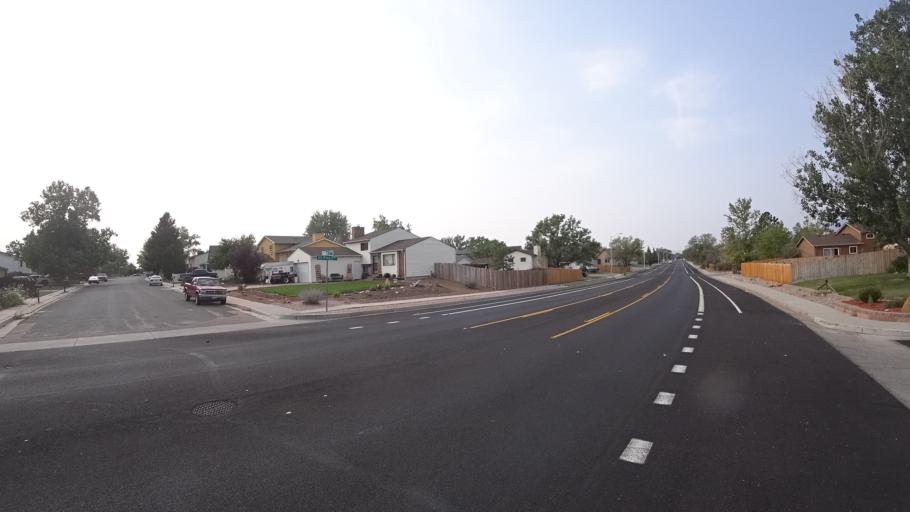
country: US
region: Colorado
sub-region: El Paso County
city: Cimarron Hills
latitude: 38.8145
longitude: -104.7372
